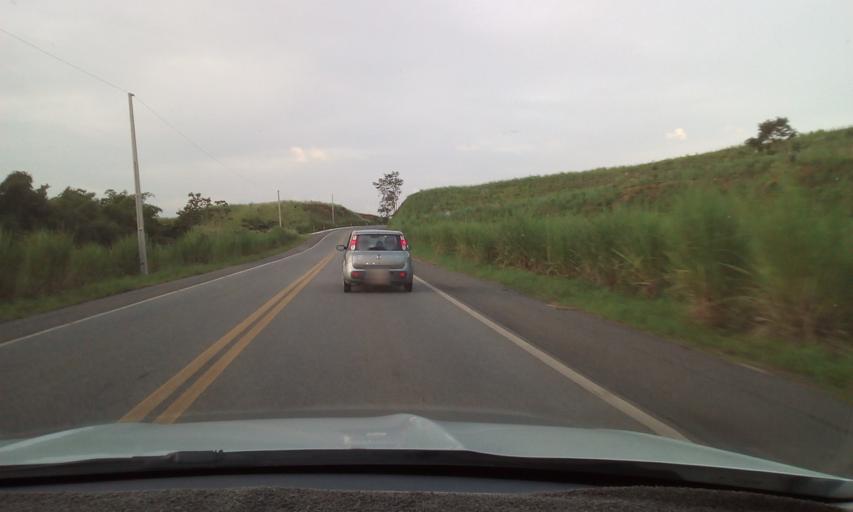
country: BR
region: Pernambuco
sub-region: Vicencia
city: Vicencia
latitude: -7.6320
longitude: -35.2512
